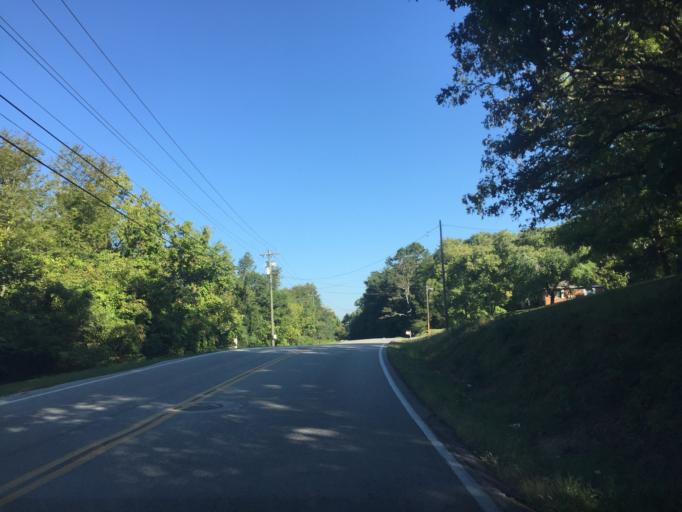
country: US
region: Tennessee
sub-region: Hamilton County
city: Harrison
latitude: 35.1171
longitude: -85.0828
